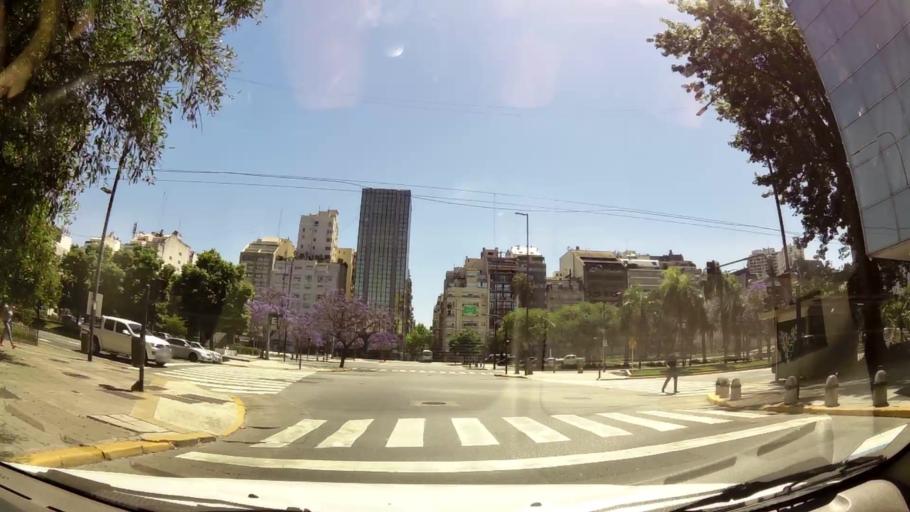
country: AR
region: Buenos Aires F.D.
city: Retiro
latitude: -34.5929
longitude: -58.3815
